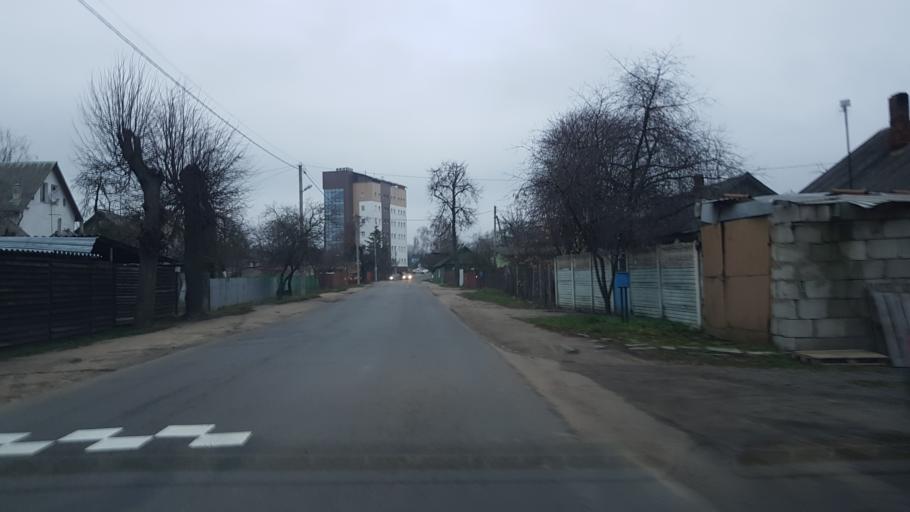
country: BY
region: Minsk
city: Minsk
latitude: 53.9380
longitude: 27.5356
